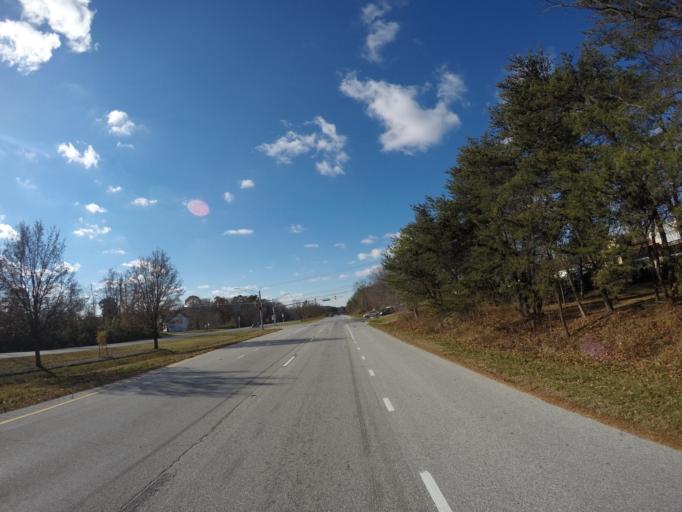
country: US
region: Maryland
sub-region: Anne Arundel County
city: Lake Shore
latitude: 39.1190
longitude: -76.5165
